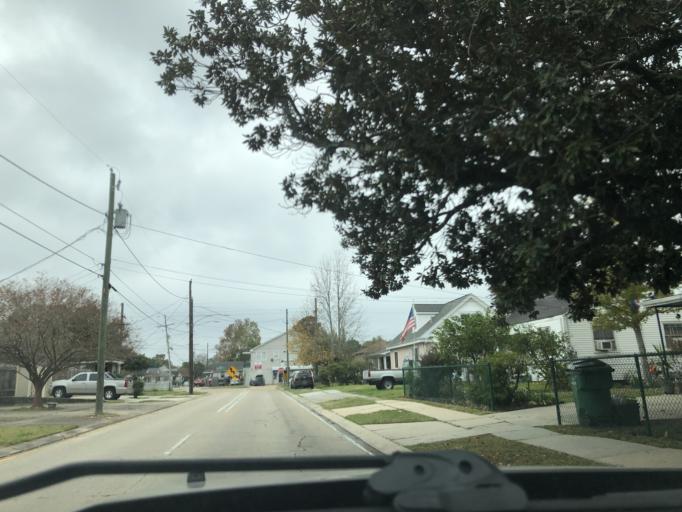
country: US
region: Louisiana
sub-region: Jefferson Parish
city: Metairie Terrace
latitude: 29.9822
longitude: -90.1605
